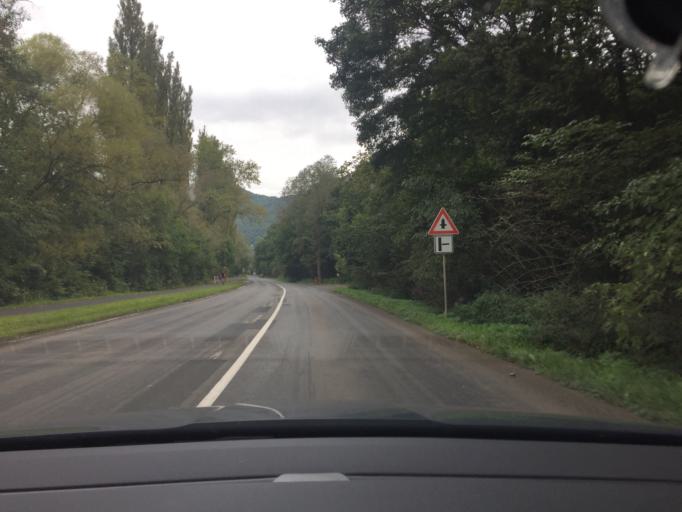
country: CZ
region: Ustecky
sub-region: Okres Usti nad Labem
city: Usti nad Labem
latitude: 50.6088
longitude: 14.0763
